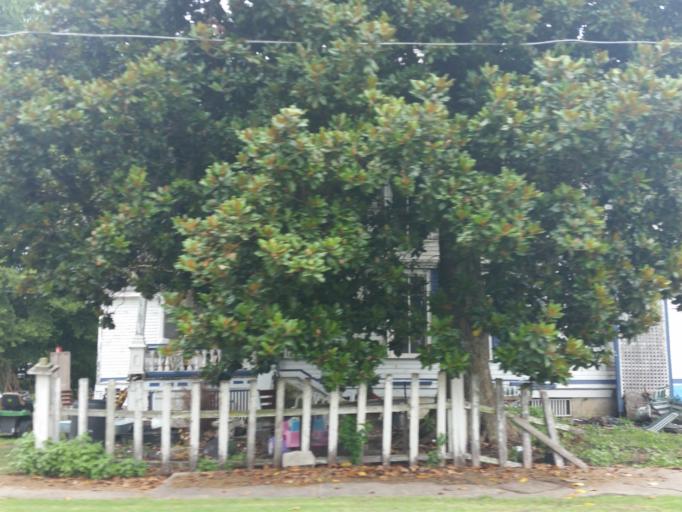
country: US
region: Illinois
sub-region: Alexander County
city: Cairo
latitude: 36.9976
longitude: -89.1674
